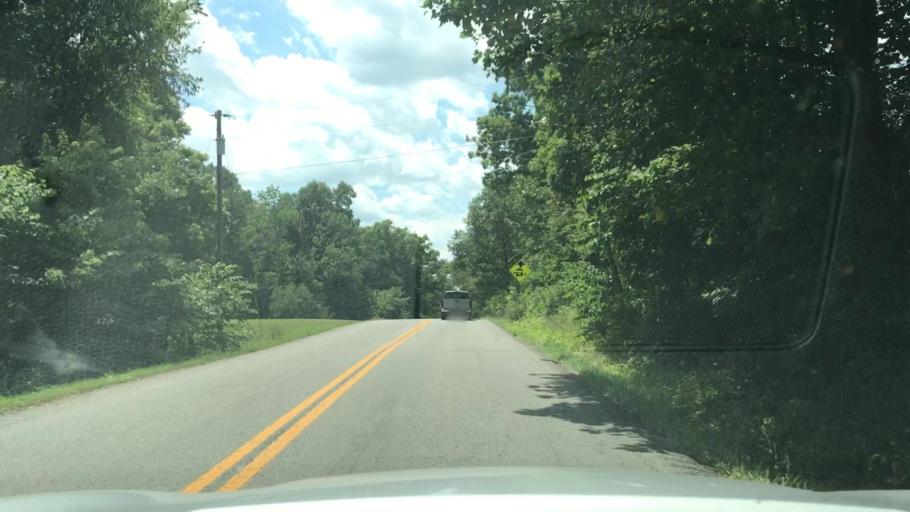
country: US
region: Kentucky
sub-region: Muhlenberg County
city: Greenville
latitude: 37.1828
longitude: -87.2307
